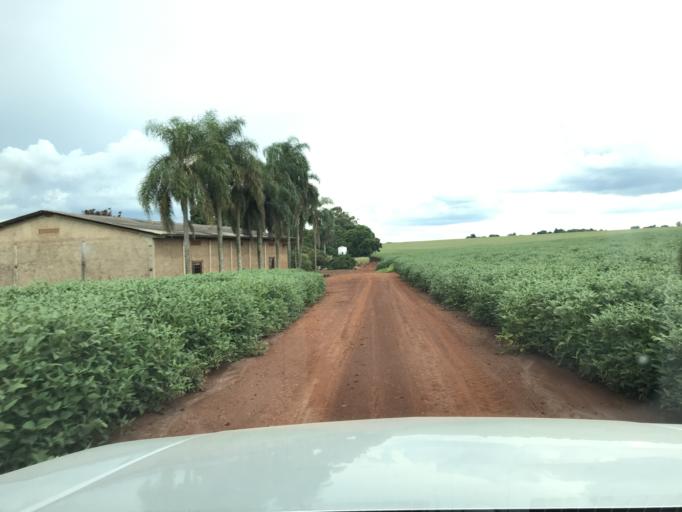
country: BR
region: Parana
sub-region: Palotina
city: Palotina
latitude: -24.2727
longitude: -53.7758
